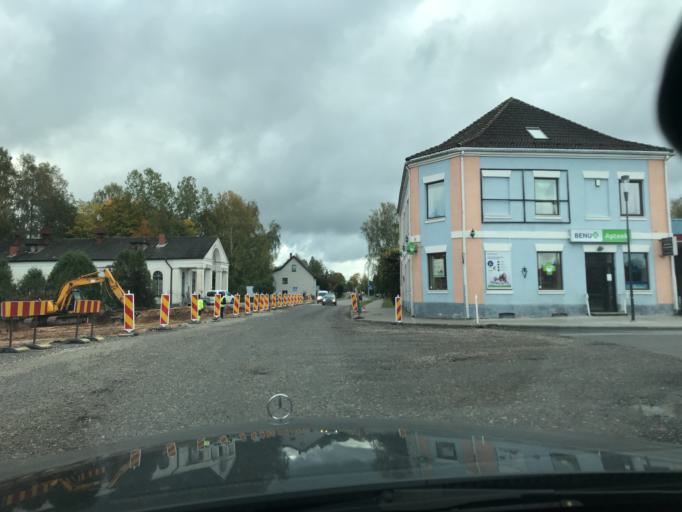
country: EE
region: Valgamaa
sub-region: Torva linn
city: Torva
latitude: 58.0026
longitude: 25.9229
